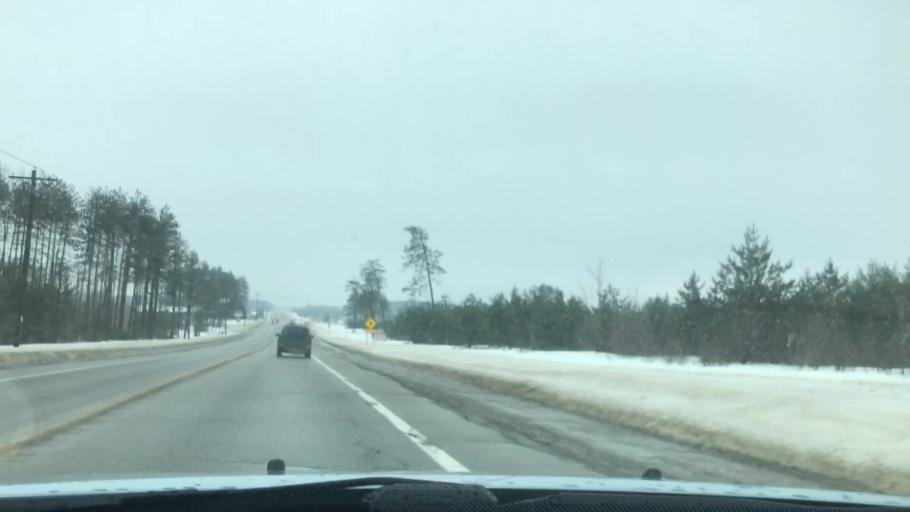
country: US
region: Michigan
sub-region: Otsego County
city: Gaylord
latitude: 45.0275
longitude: -84.7313
